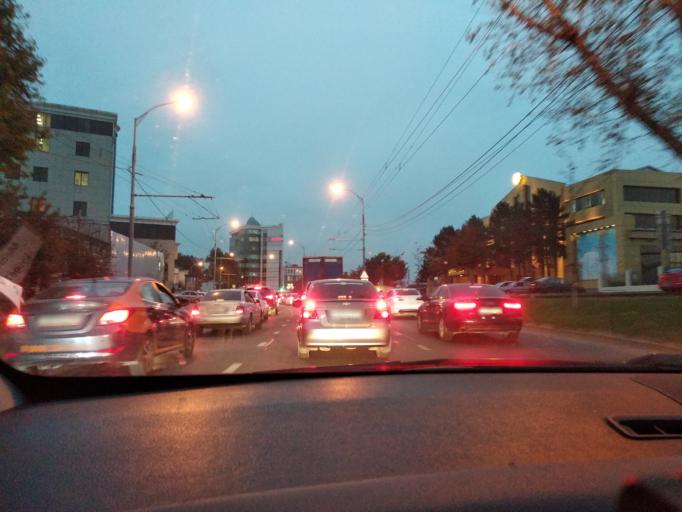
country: RU
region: Krasnodarskiy
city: Krasnodar
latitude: 45.0130
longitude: 38.9786
